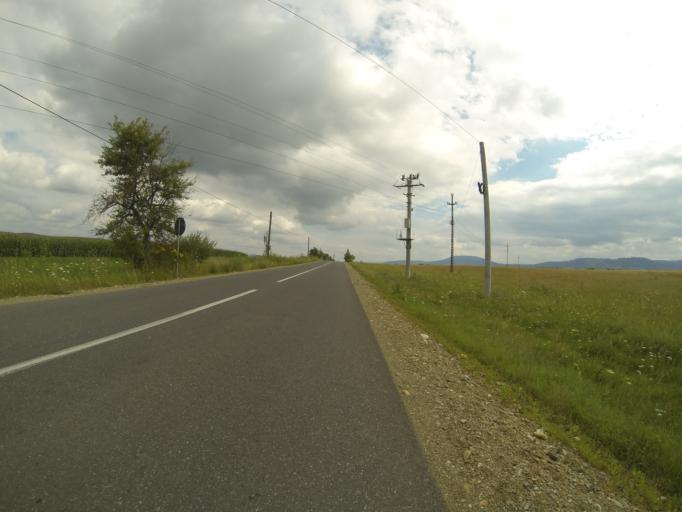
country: RO
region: Brasov
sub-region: Comuna Parau
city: Parau
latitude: 45.8568
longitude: 25.1963
